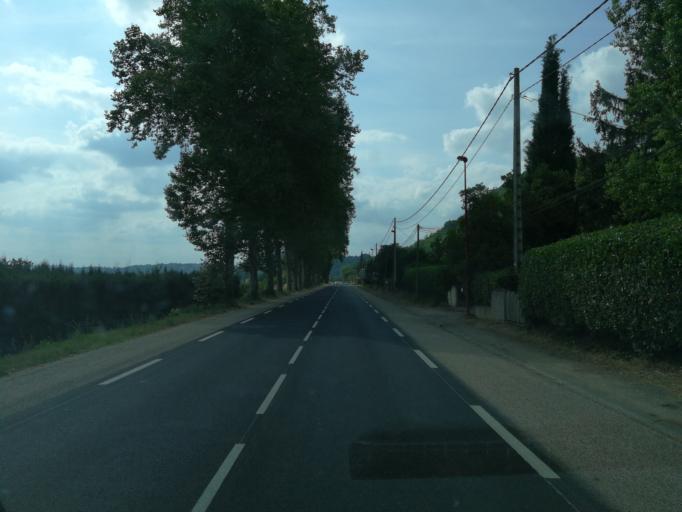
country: FR
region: Aquitaine
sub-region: Departement du Lot-et-Garonne
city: Montayral
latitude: 44.4925
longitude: 1.0020
